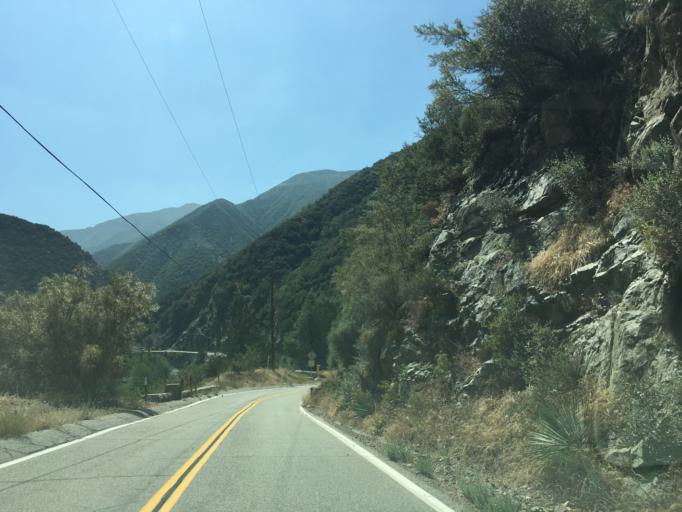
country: US
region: California
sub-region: Los Angeles County
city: San Dimas
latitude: 34.2296
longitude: -117.7735
